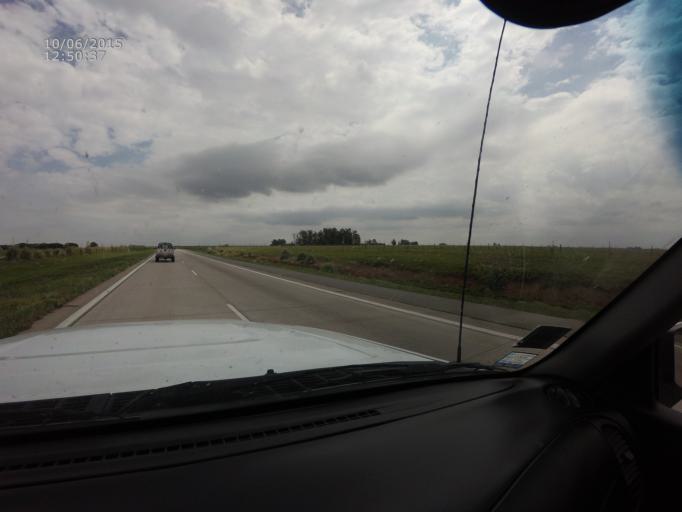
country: AR
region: Santa Fe
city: Canada de Gomez
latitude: -32.8285
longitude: -61.4955
